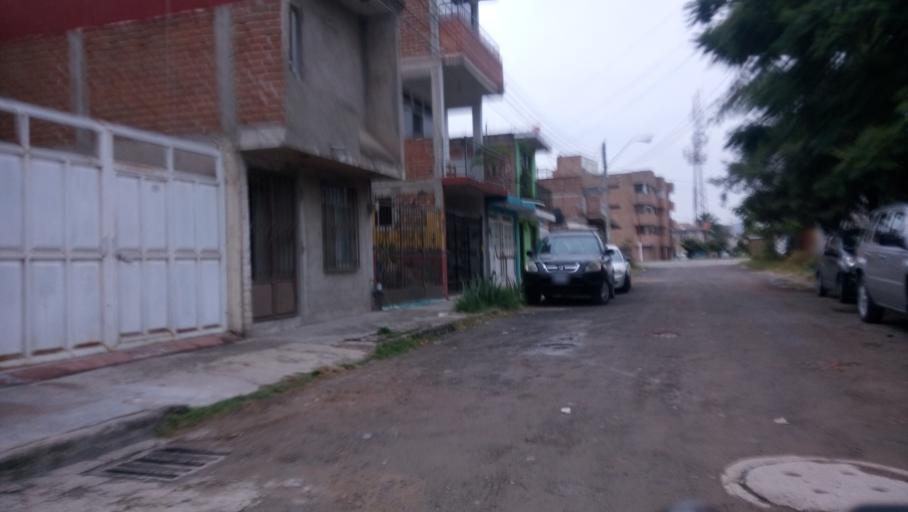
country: MX
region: Guanajuato
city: Leon
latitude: 21.1489
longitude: -101.6637
